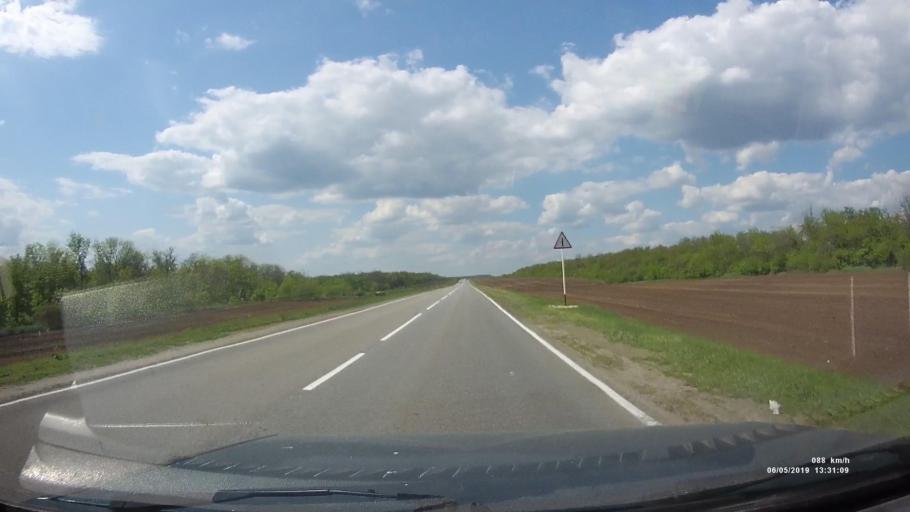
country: RU
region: Rostov
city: Ust'-Donetskiy
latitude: 47.6747
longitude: 40.8148
